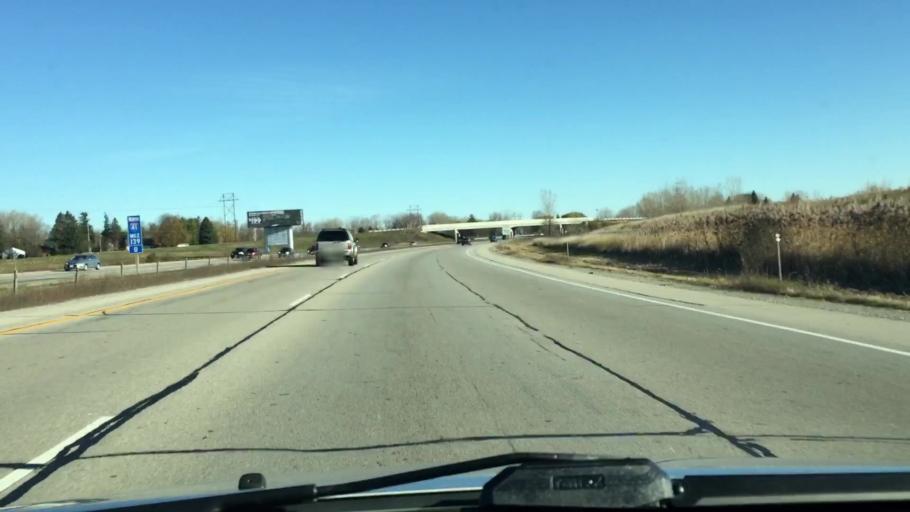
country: US
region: Wisconsin
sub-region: Outagamie County
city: Appleton
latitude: 44.2919
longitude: -88.4654
